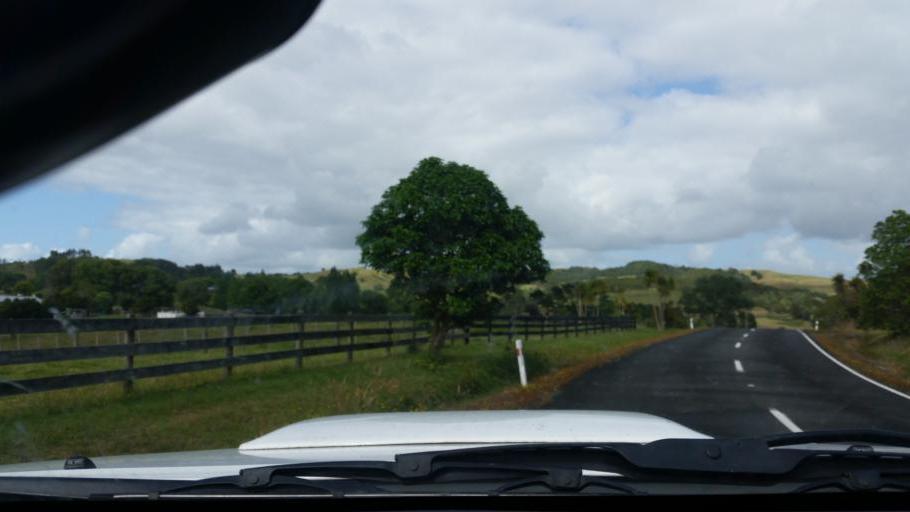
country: NZ
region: Auckland
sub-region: Auckland
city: Wellsford
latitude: -36.1318
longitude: 174.3651
